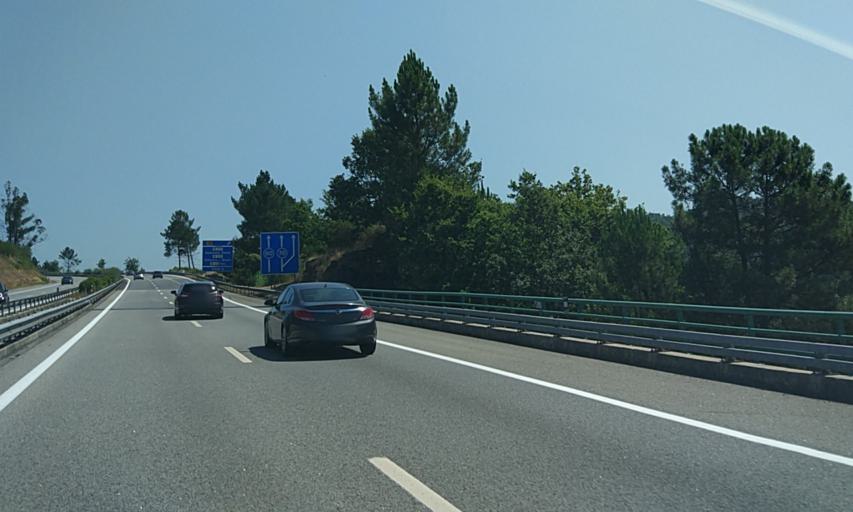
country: PT
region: Porto
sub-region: Amarante
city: Amarante
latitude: 41.2567
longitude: -8.1290
